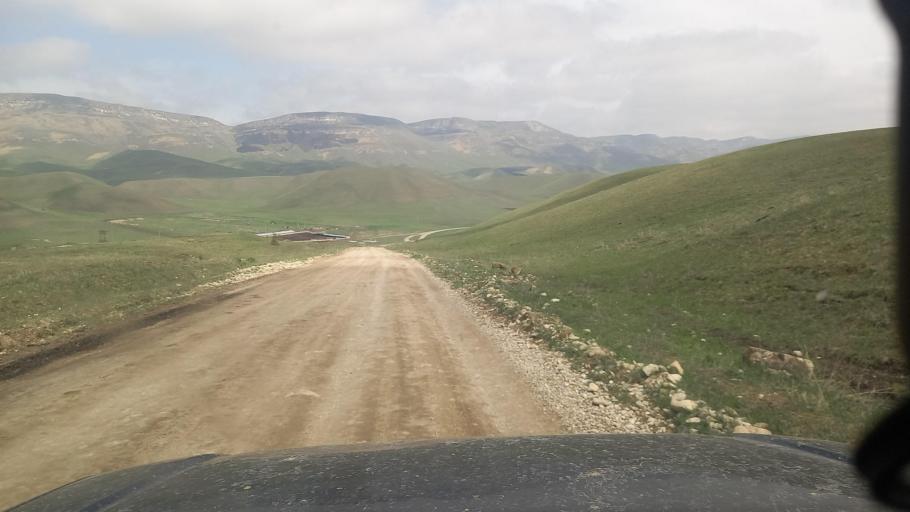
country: RU
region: Kabardino-Balkariya
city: Kamennomostskoye
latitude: 43.7966
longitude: 42.8998
